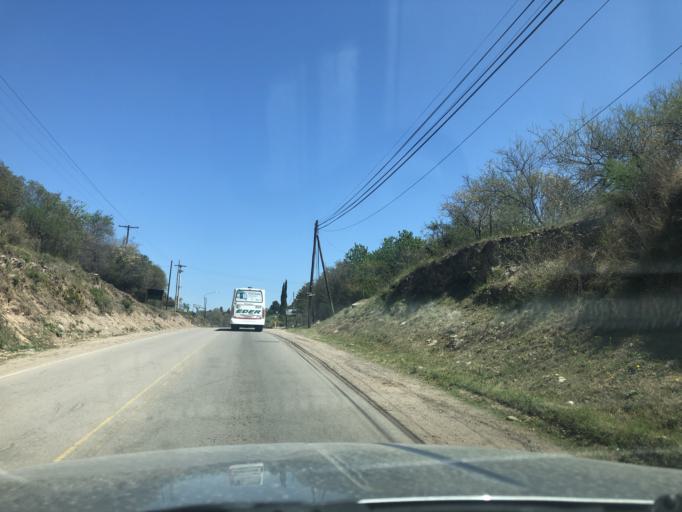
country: AR
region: Cordoba
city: La Granja
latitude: -31.0167
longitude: -64.2726
